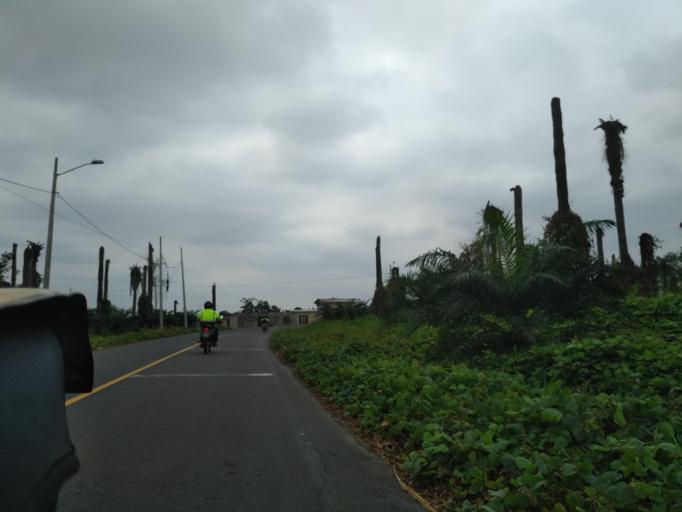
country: EC
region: Los Rios
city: Quevedo
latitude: -1.0235
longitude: -79.4366
